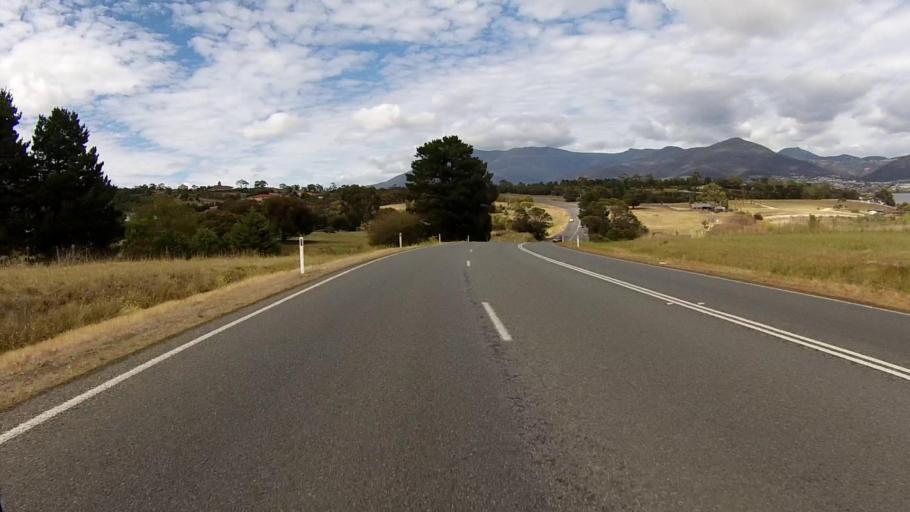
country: AU
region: Tasmania
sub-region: Brighton
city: Old Beach
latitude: -42.7937
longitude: 147.2928
